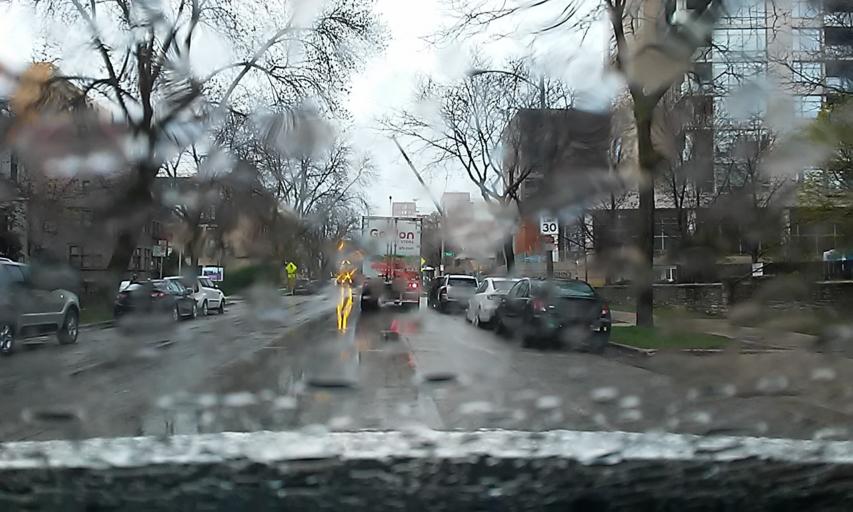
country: US
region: Wisconsin
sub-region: Milwaukee County
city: Milwaukee
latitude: 43.0529
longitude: -87.8906
